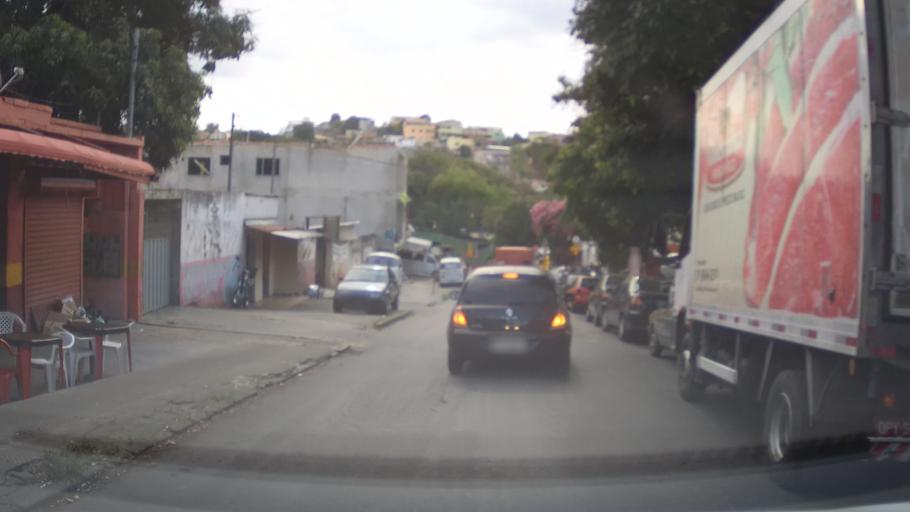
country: BR
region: Minas Gerais
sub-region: Belo Horizonte
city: Belo Horizonte
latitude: -19.8660
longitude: -43.9026
